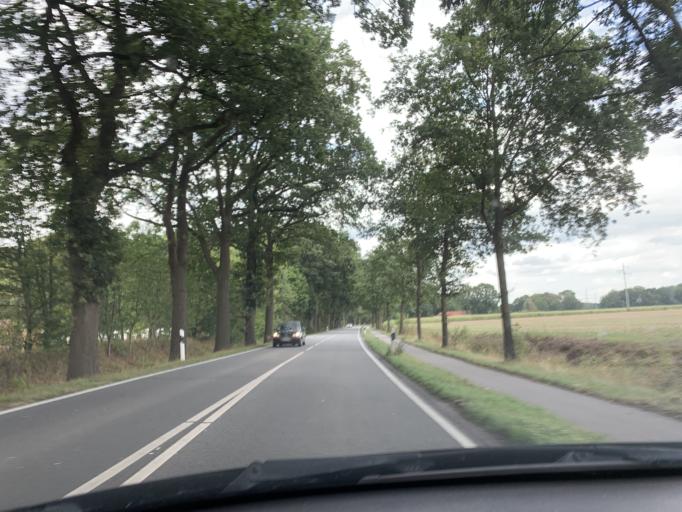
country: DE
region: Lower Saxony
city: Westerstede
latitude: 53.2354
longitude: 7.9062
